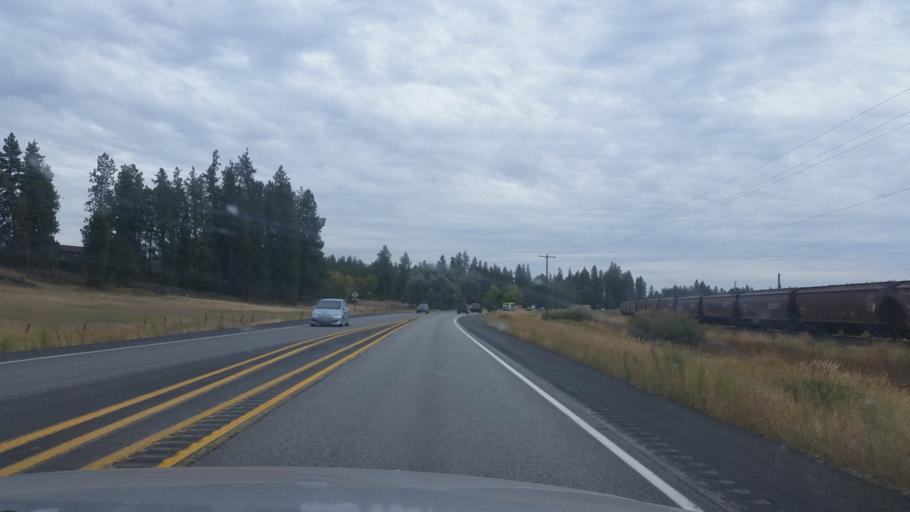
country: US
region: Washington
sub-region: Spokane County
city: Cheney
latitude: 47.5286
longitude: -117.5685
